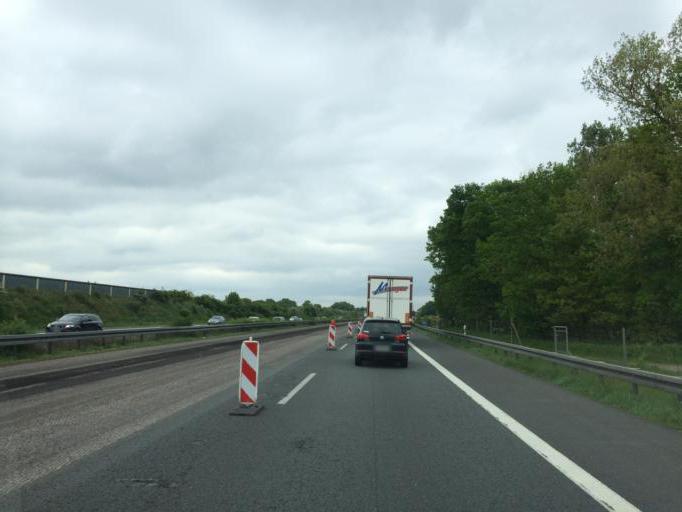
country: DE
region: Lower Saxony
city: Klein Schwulper
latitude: 52.3293
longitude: 10.4546
